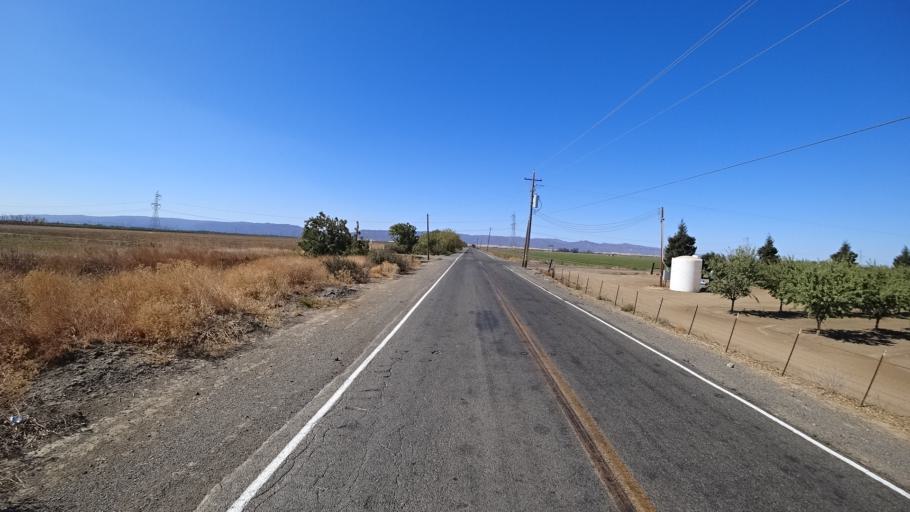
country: US
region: California
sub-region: Yolo County
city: Winters
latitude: 38.5618
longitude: -121.9046
